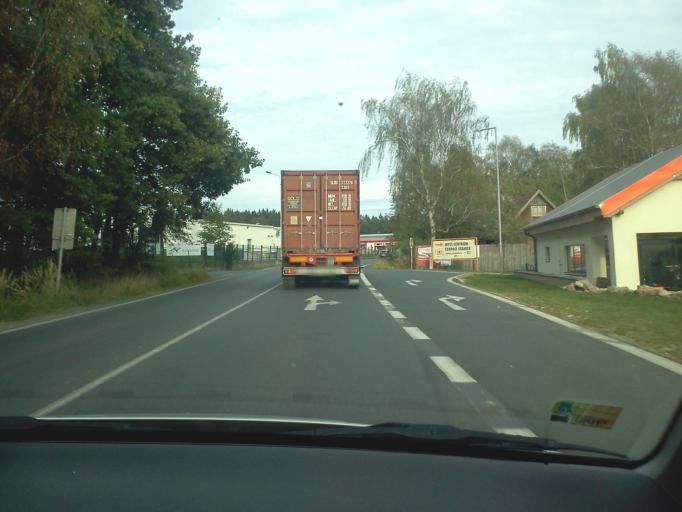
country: CZ
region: Central Bohemia
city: Mukarov
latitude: 49.9901
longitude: 14.7220
